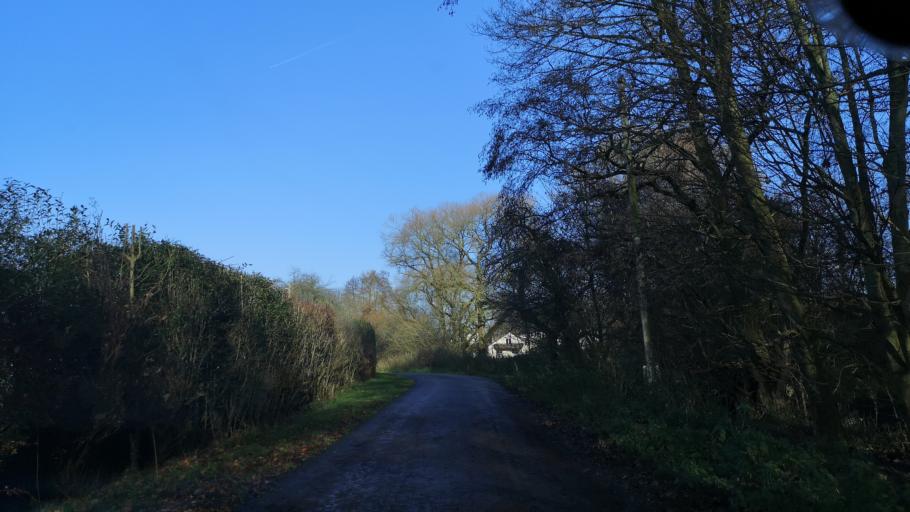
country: DE
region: Hesse
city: Ober-Ramstadt
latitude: 49.7866
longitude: 8.7433
